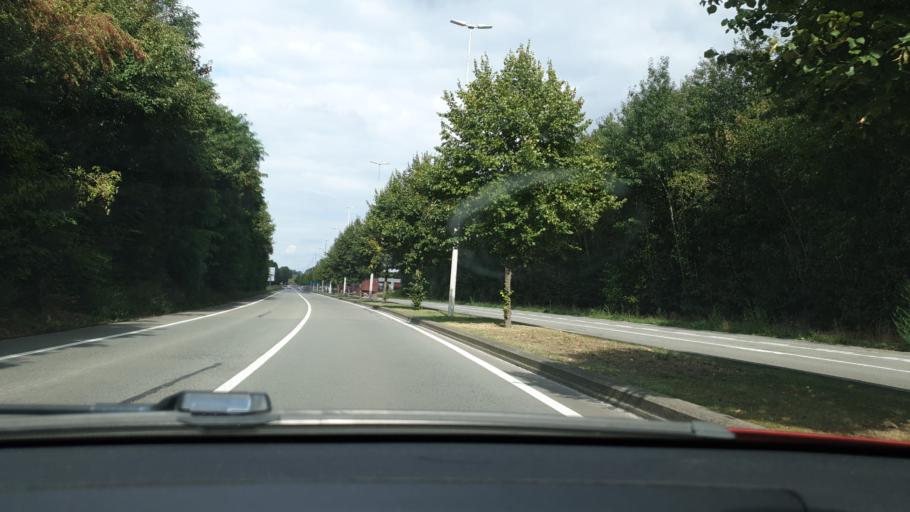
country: BE
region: Wallonia
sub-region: Province du Hainaut
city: Ath
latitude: 50.6322
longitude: 3.7590
